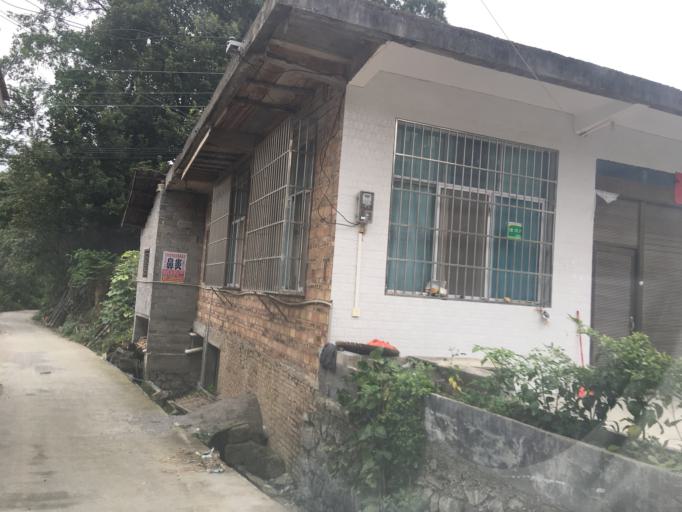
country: CN
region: Guangxi Zhuangzu Zizhiqu
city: Xinzhou
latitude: 25.1553
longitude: 105.6959
